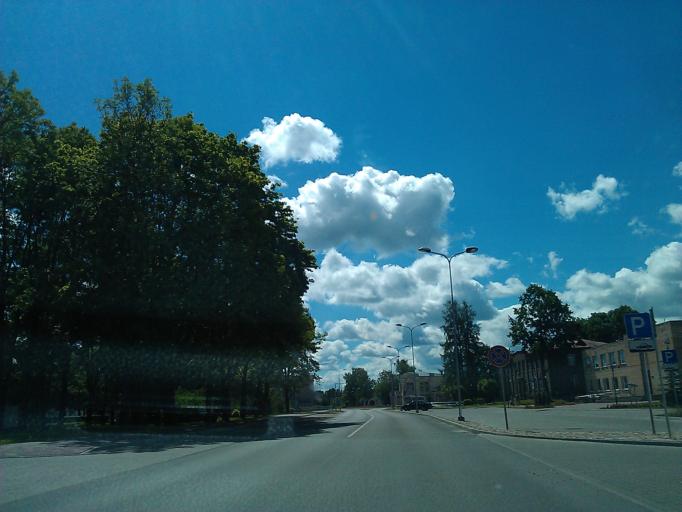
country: LV
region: Vilanu
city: Vilani
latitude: 56.5519
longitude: 26.9220
